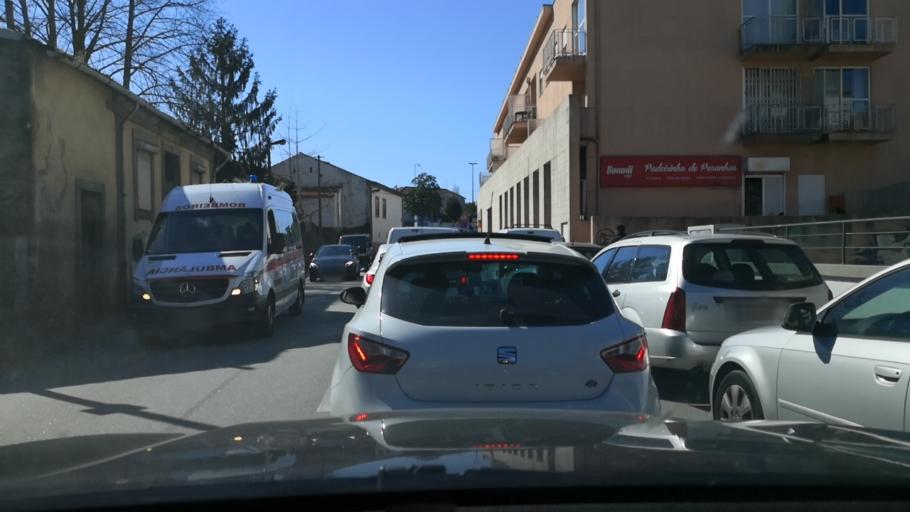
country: PT
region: Porto
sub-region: Porto
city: Porto
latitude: 41.1737
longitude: -8.6042
